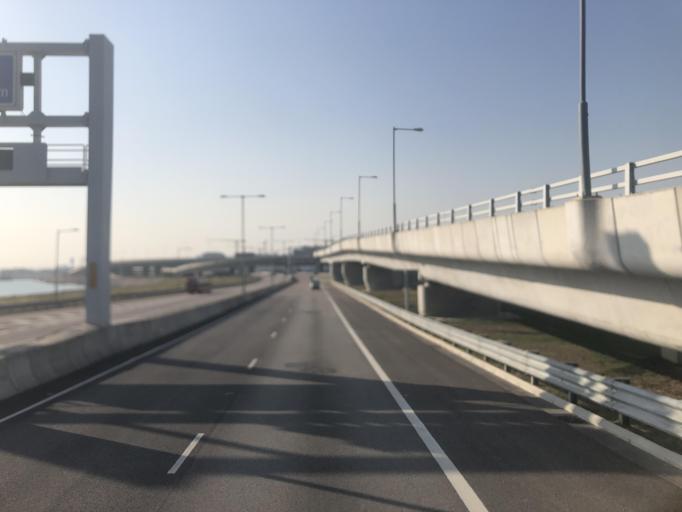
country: HK
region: Tuen Mun
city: Tuen Mun
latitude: 22.3135
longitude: 113.9508
